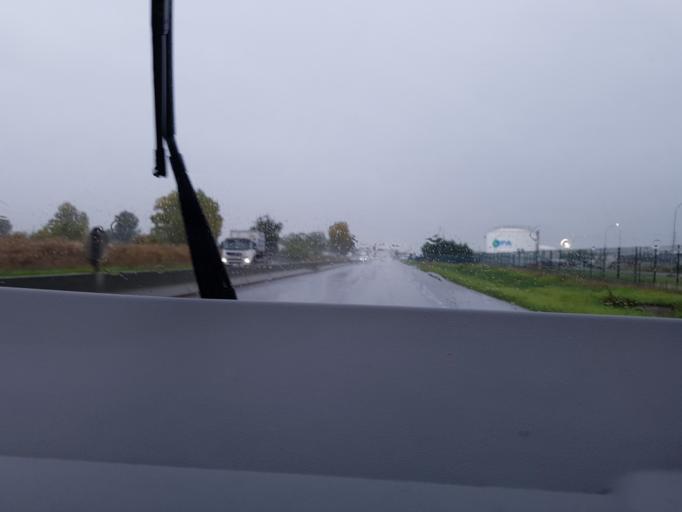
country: FR
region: Aquitaine
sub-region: Departement de la Gironde
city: Bassens
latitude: 44.9212
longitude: -0.5380
